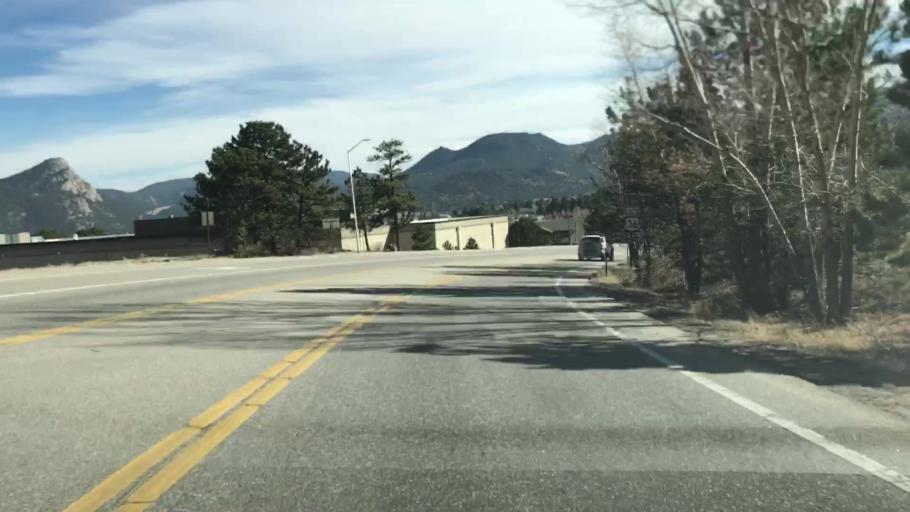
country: US
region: Colorado
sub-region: Larimer County
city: Estes Park
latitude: 40.3806
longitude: -105.5183
